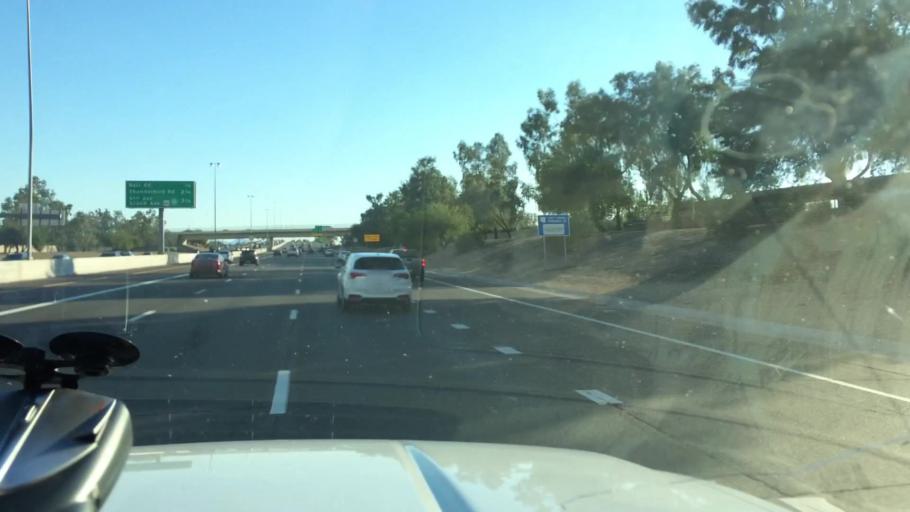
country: US
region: Arizona
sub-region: Maricopa County
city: Sun City
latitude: 33.6464
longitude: -112.2345
